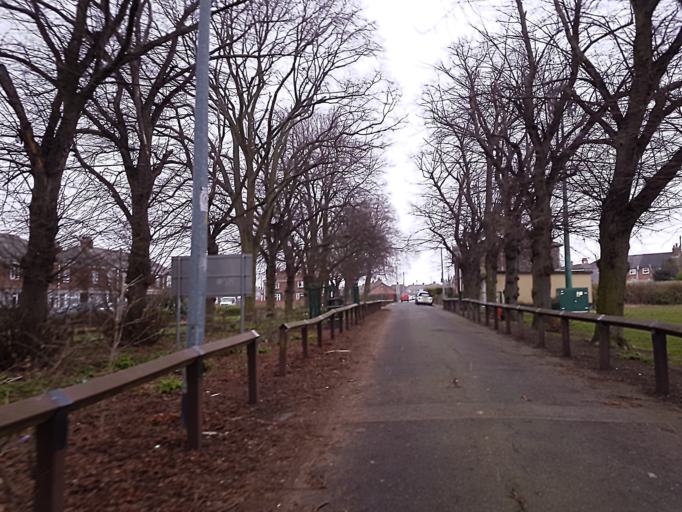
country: GB
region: England
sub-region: North East Lincolnshire
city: Grimbsy
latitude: 53.5599
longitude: -0.1091
